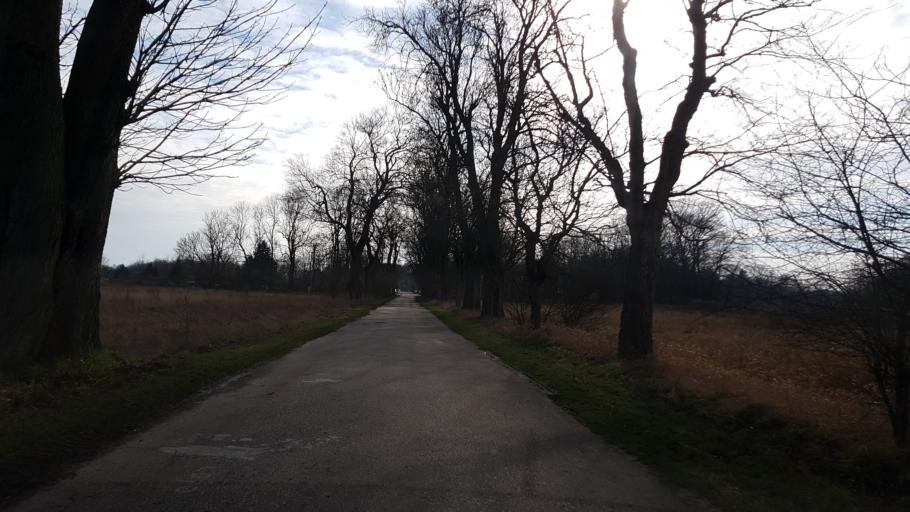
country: PL
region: West Pomeranian Voivodeship
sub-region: Powiat policki
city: Dobra
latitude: 53.5618
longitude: 14.3172
